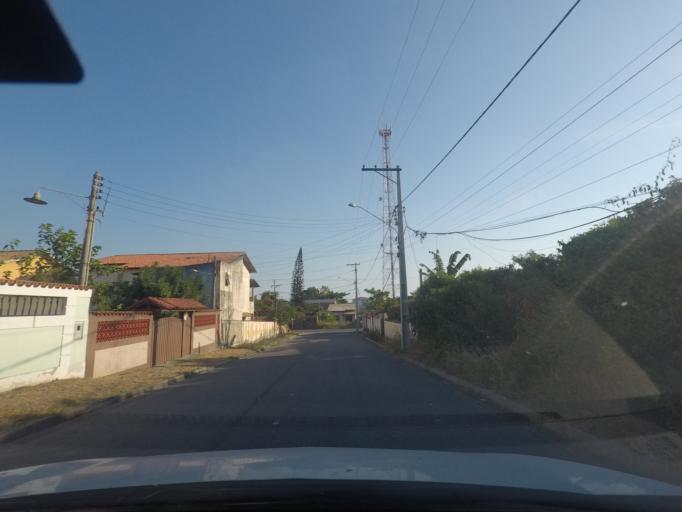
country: BR
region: Rio de Janeiro
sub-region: Marica
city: Marica
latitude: -22.9697
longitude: -42.9343
